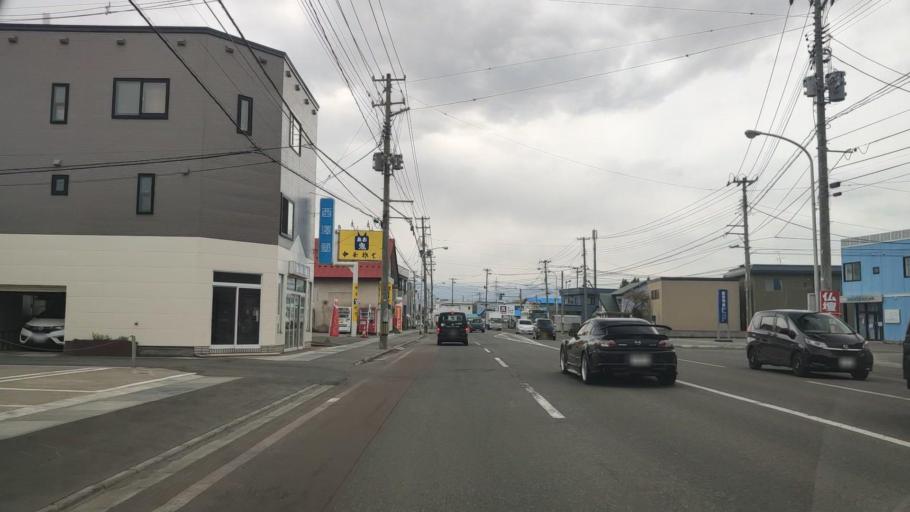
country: JP
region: Aomori
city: Aomori Shi
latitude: 40.8145
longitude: 140.7760
